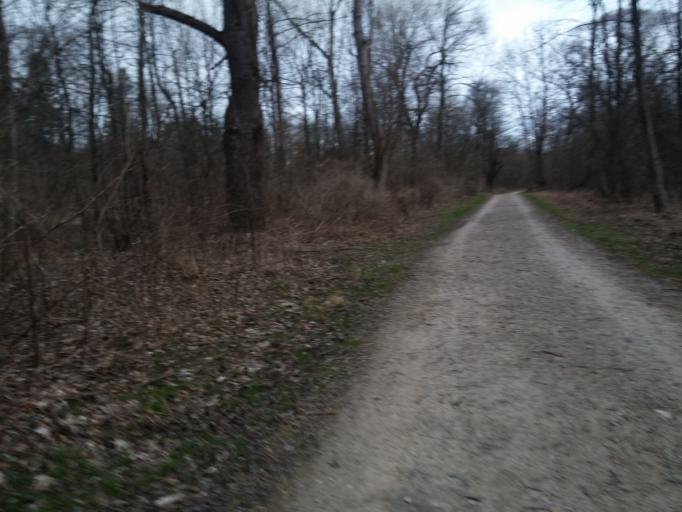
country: DE
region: Bavaria
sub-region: Upper Bavaria
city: Ismaning
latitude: 48.2296
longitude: 11.6634
